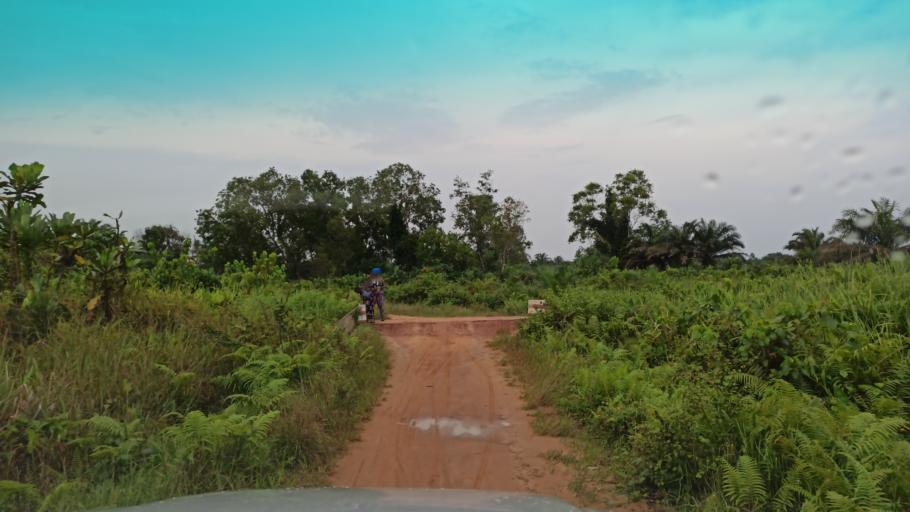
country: BJ
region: Queme
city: Porto-Novo
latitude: 6.4610
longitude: 2.6755
